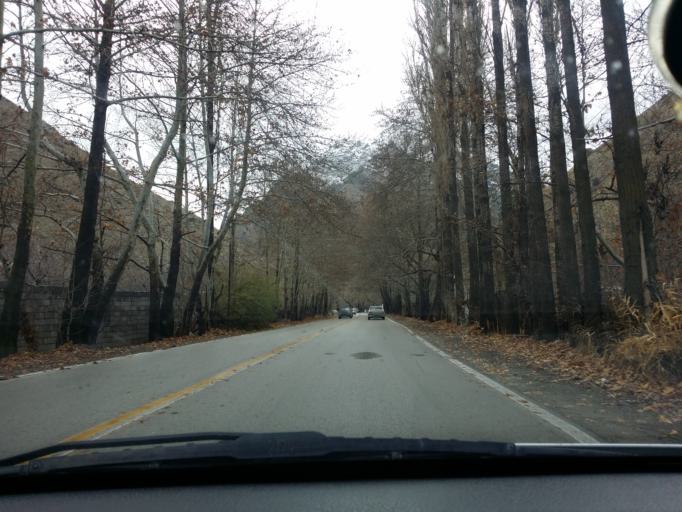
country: IR
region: Tehran
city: Tajrish
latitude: 36.0279
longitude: 51.2429
